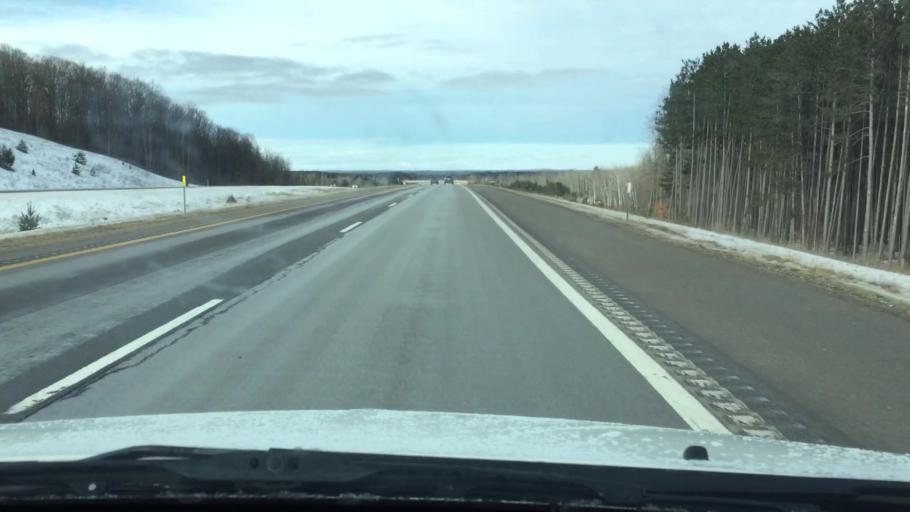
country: US
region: Michigan
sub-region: Wexford County
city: Manton
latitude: 44.4421
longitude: -85.3948
